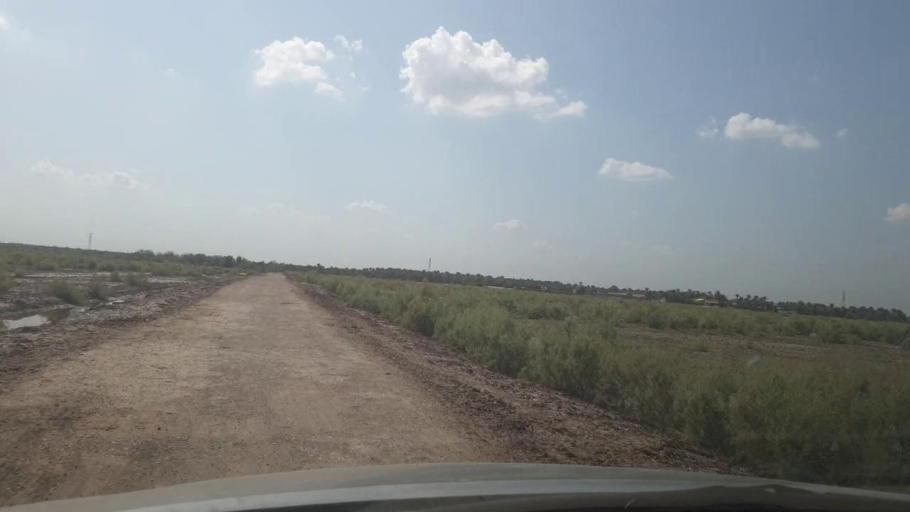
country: PK
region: Sindh
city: Khairpur
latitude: 27.5481
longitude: 68.8173
